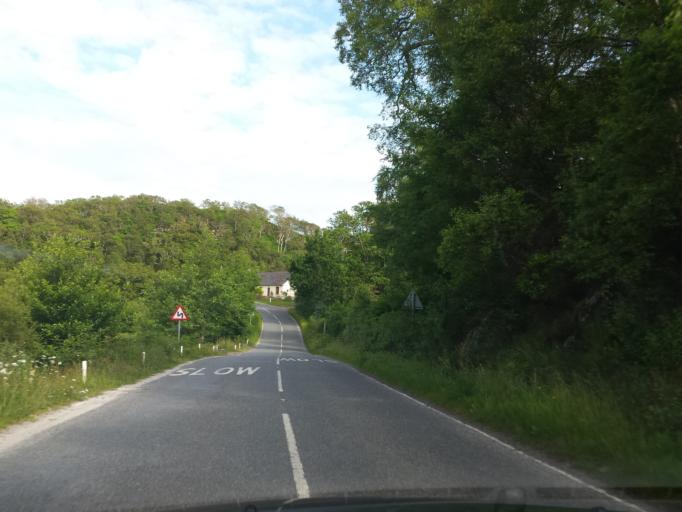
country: GB
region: Scotland
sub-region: Argyll and Bute
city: Isle Of Mull
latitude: 56.9607
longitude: -5.8229
